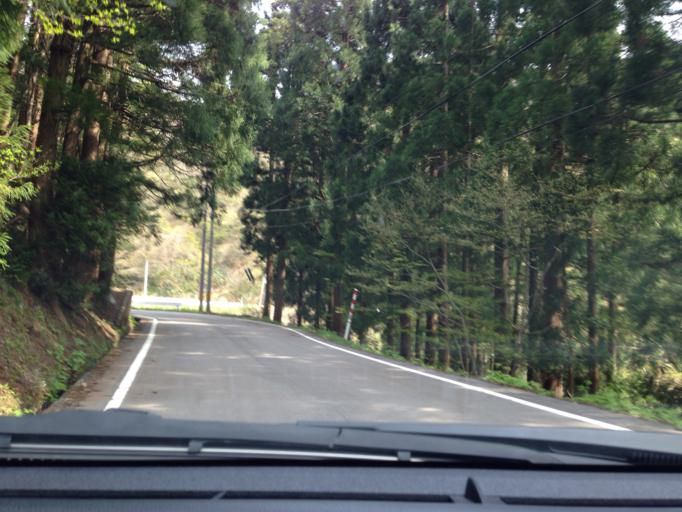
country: JP
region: Toyama
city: Fukumitsu
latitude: 36.4783
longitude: 136.8112
